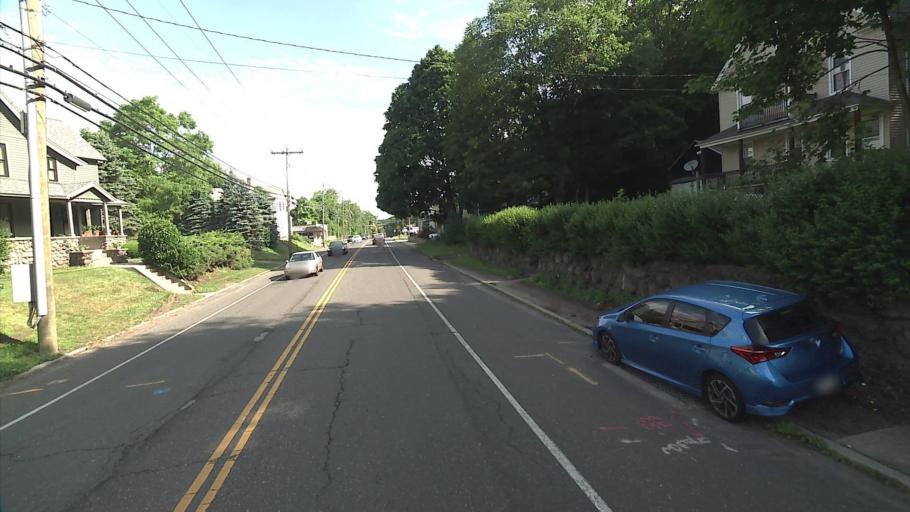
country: US
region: Connecticut
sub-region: New Haven County
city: Naugatuck
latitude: 41.4791
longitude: -73.0479
